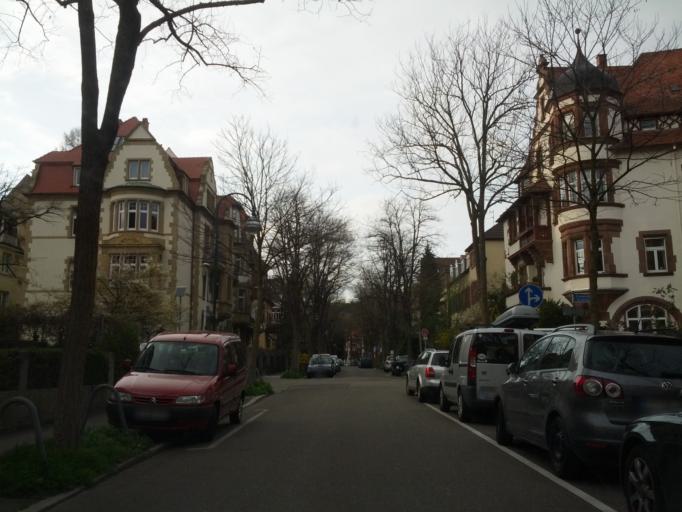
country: DE
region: Baden-Wuerttemberg
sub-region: Freiburg Region
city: Freiburg
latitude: 47.9856
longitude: 7.8601
